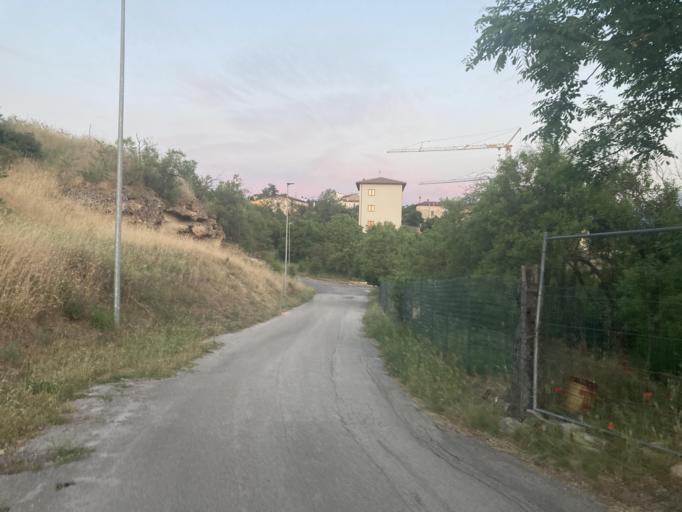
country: IT
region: Abruzzo
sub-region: Provincia dell' Aquila
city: San Demetrio Ne' Vestini
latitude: 42.2927
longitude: 13.5526
